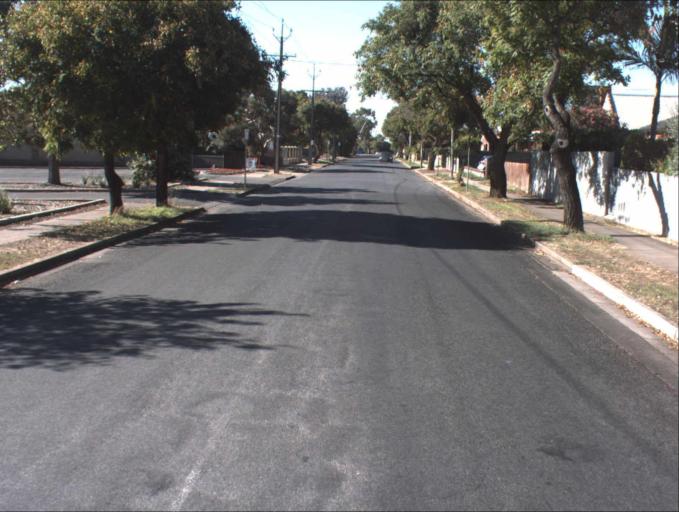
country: AU
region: South Australia
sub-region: Prospect
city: Prospect
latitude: -34.8777
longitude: 138.6040
